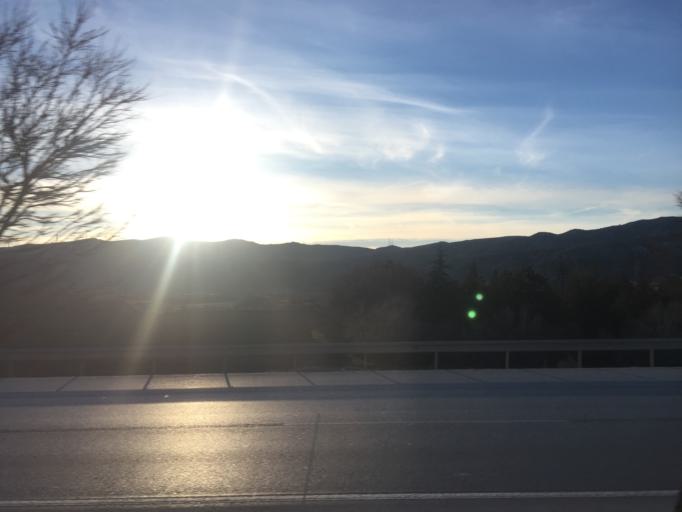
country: TR
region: Kirikkale
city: Yahsihan
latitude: 39.9151
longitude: 33.4320
